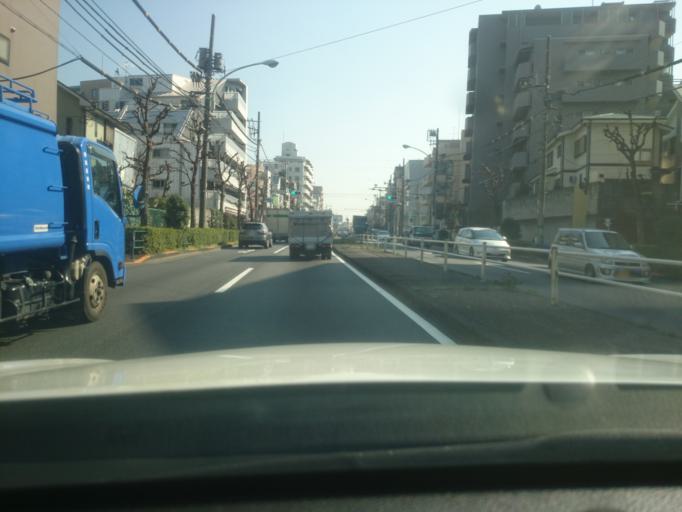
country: JP
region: Tokyo
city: Musashino
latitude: 35.7006
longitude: 139.6170
